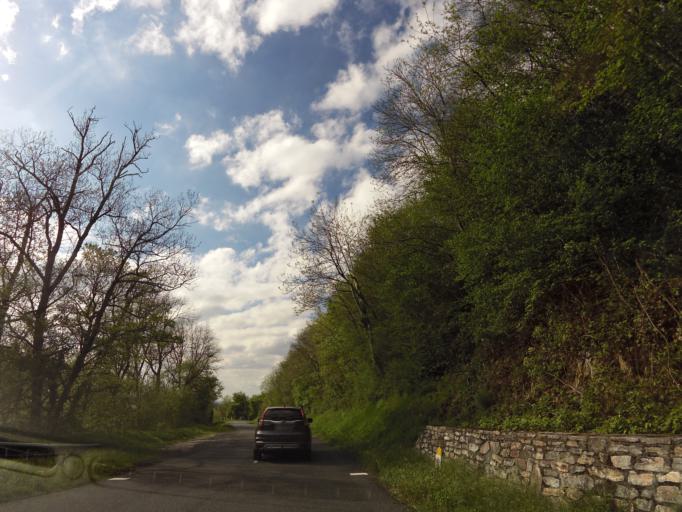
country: FR
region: Midi-Pyrenees
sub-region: Departement du Tarn
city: Soreze
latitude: 43.4288
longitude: 2.0558
